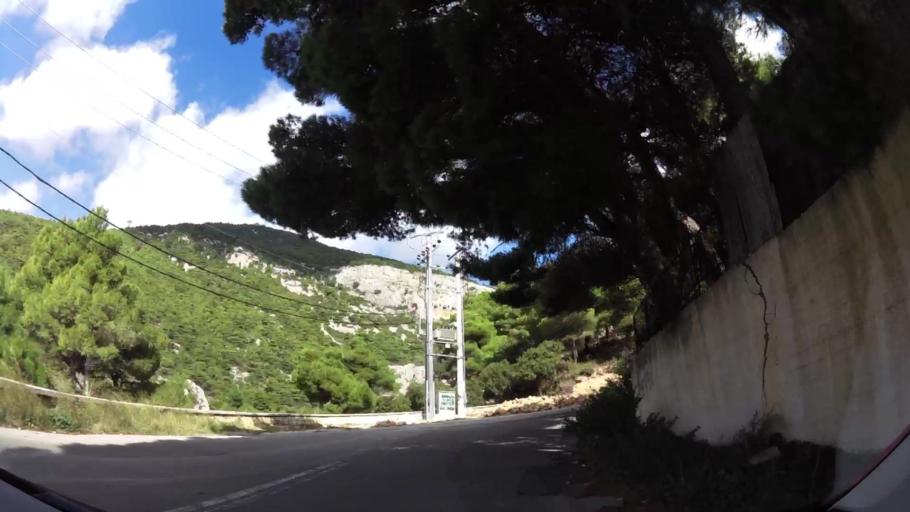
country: GR
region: Attica
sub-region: Nomarchia Anatolikis Attikis
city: Thrakomakedones
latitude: 38.1441
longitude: 23.7453
